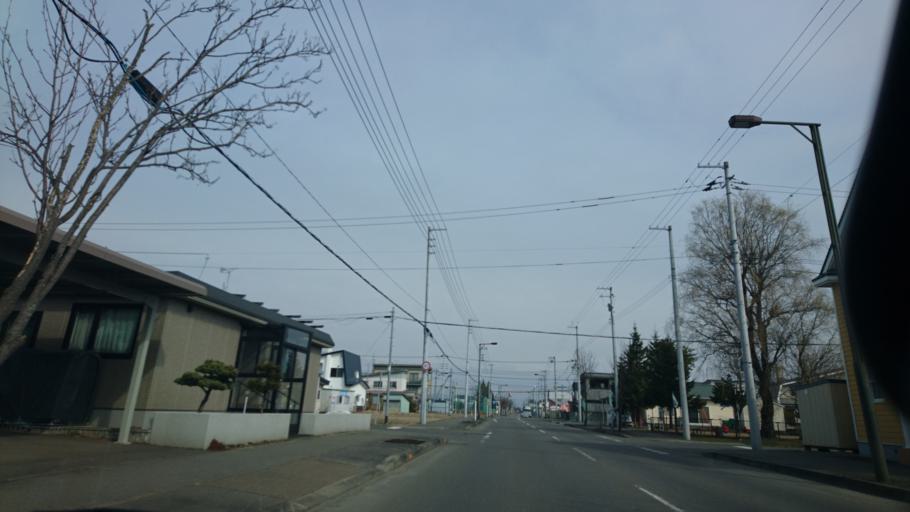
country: JP
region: Hokkaido
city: Otofuke
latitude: 42.9666
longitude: 143.2131
